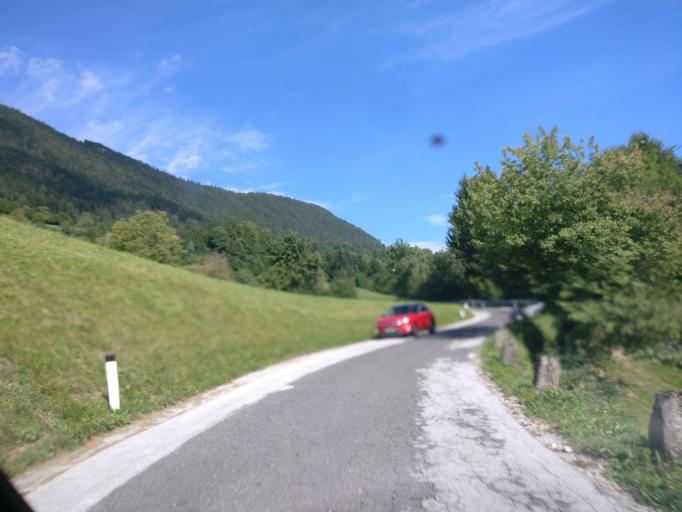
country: SI
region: Zelezniki
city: Zelezniki
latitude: 46.2507
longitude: 14.1676
